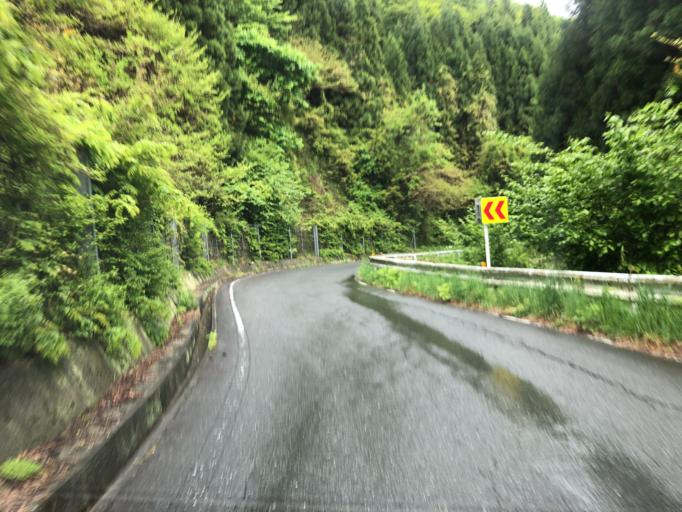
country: JP
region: Fukushima
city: Ishikawa
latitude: 37.0011
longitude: 140.6062
